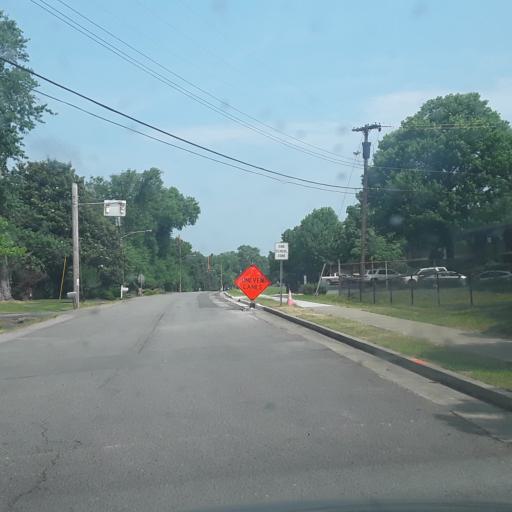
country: US
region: Tennessee
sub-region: Davidson County
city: Oak Hill
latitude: 36.0773
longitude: -86.7497
